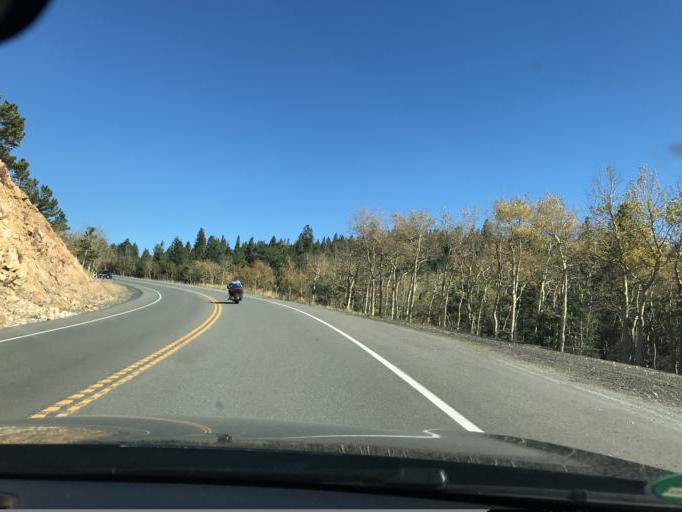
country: US
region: Colorado
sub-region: Boulder County
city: Nederland
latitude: 40.0692
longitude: -105.5140
